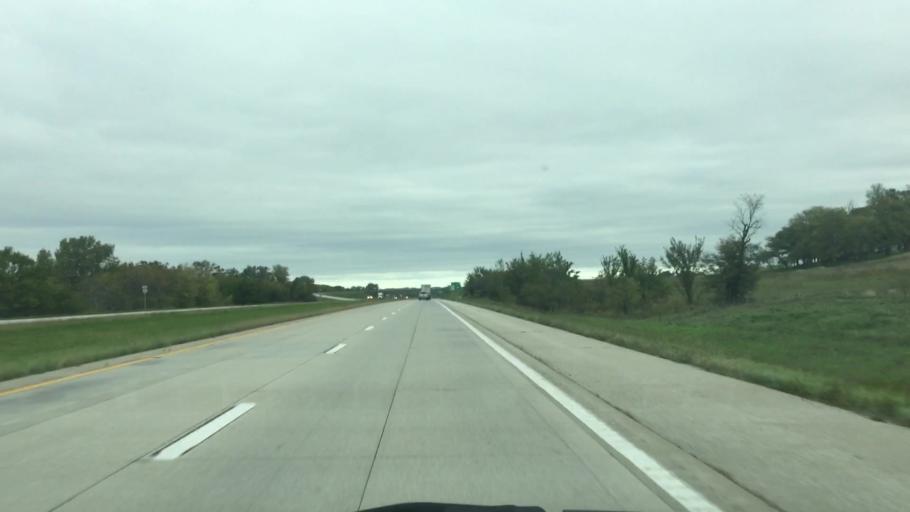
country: US
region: Missouri
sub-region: Daviess County
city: Gallatin
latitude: 39.9893
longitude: -94.0950
